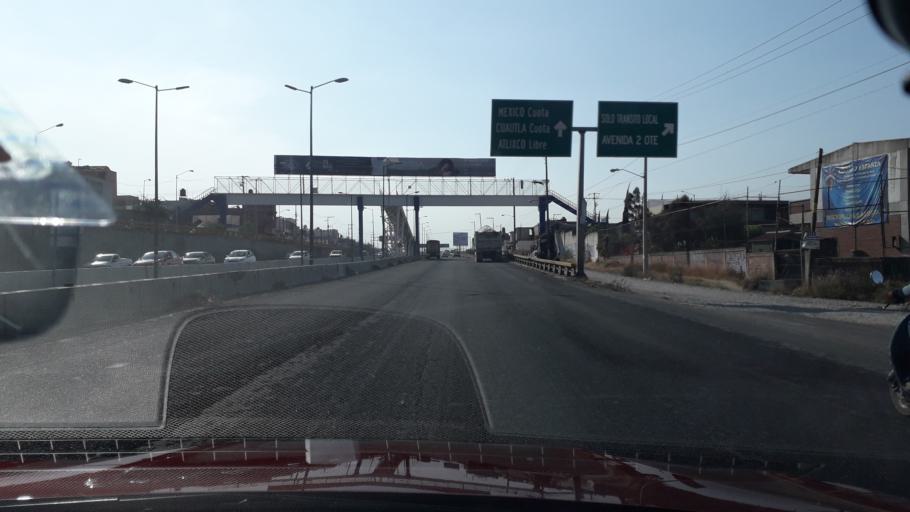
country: MX
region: Puebla
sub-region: Puebla
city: El Capulo (La Quebradora)
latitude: 18.9818
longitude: -98.2255
